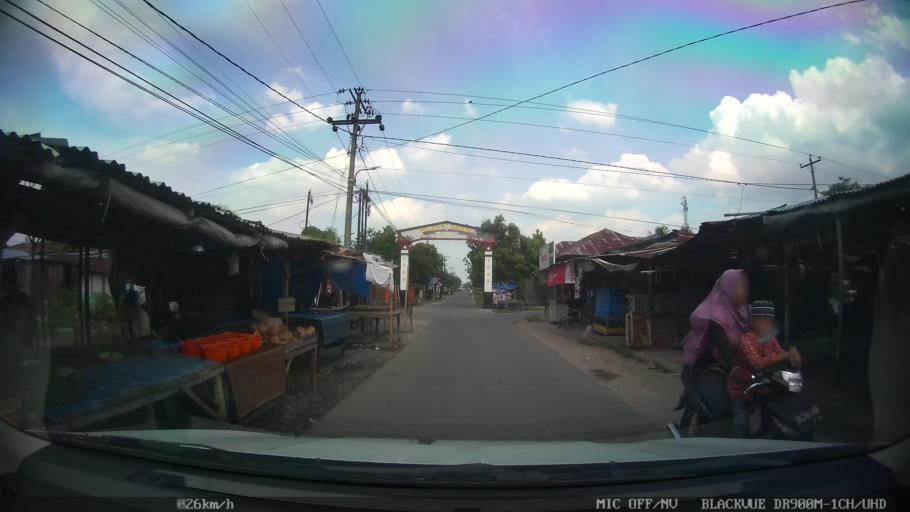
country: ID
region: North Sumatra
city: Binjai
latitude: 3.6133
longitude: 98.5259
